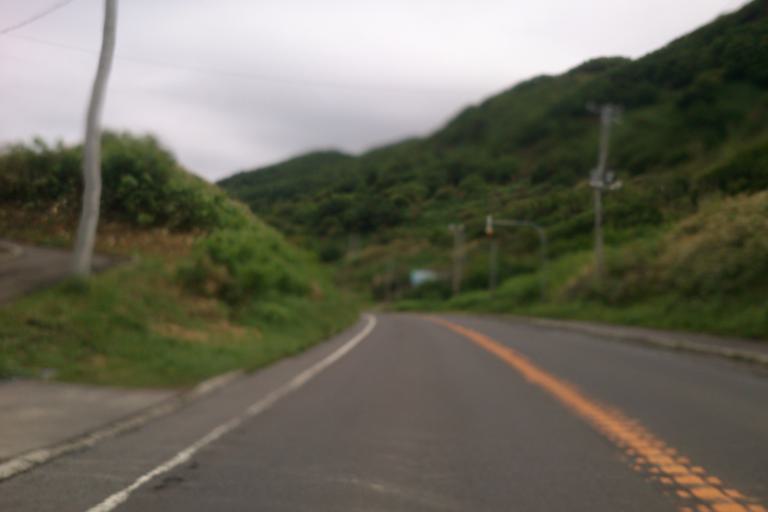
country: JP
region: Hokkaido
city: Ishikari
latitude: 43.4196
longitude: 141.4296
